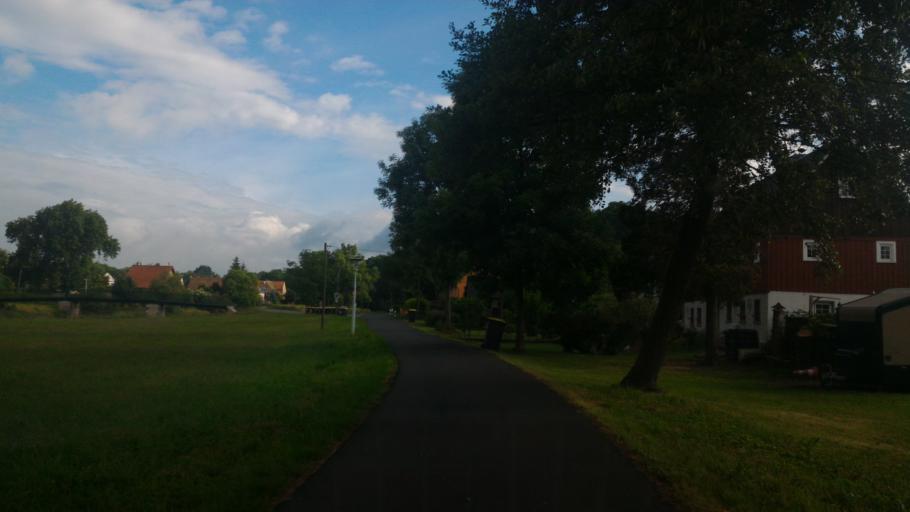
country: DE
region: Saxony
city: Mittelherwigsdorf
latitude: 50.9186
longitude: 14.7470
